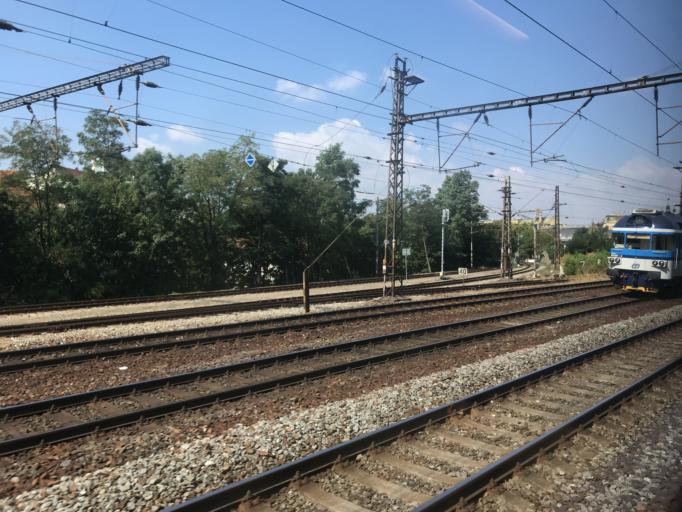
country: CZ
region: Praha
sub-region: Praha 2
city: Vysehrad
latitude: 50.0668
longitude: 14.4404
